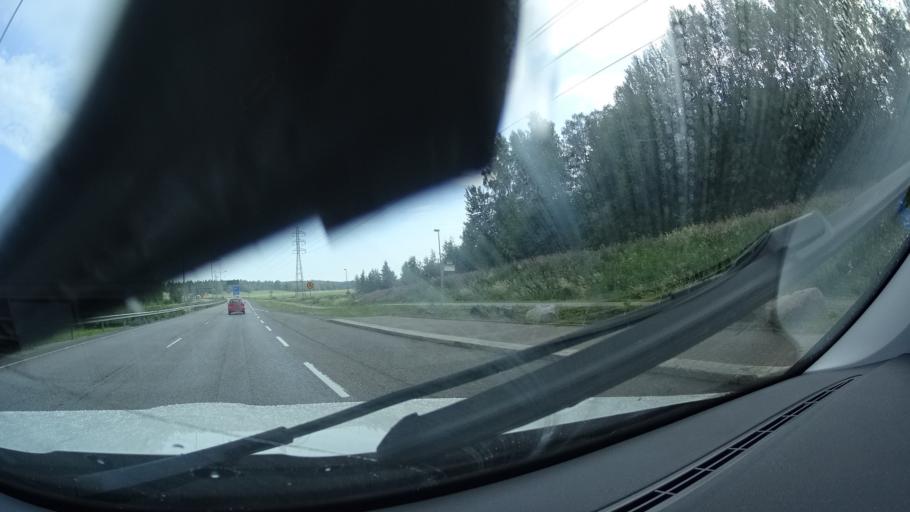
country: FI
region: Uusimaa
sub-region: Helsinki
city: Vantaa
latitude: 60.2541
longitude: 25.1306
